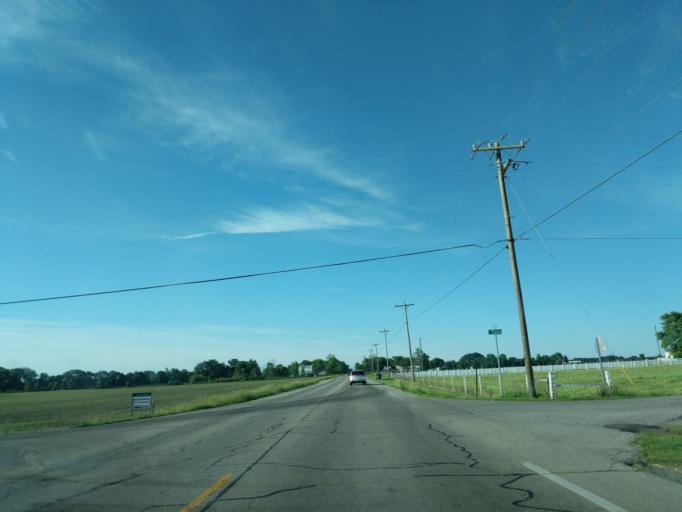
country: US
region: Indiana
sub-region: Madison County
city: Ingalls
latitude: 39.8867
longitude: -85.7705
